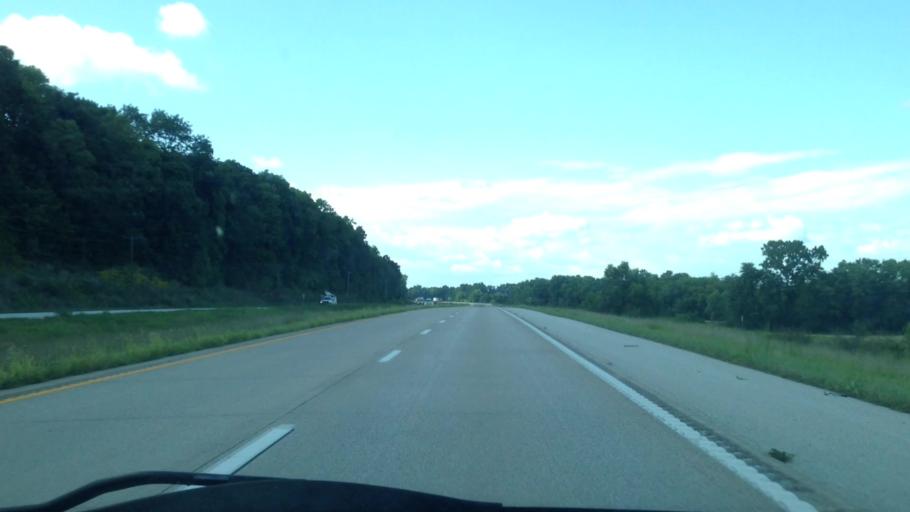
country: US
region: Missouri
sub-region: Lewis County
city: Canton
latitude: 40.2316
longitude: -91.5314
